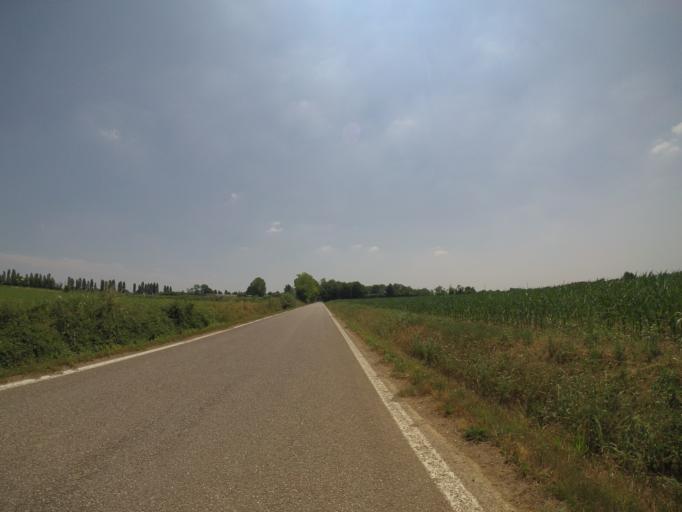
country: IT
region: Friuli Venezia Giulia
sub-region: Provincia di Udine
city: Codroipo
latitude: 45.9600
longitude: 13.0057
